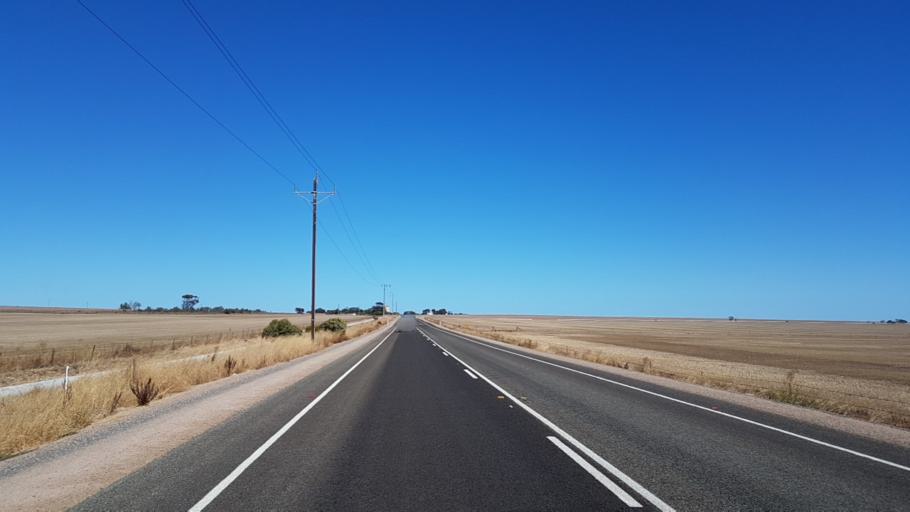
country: AU
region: South Australia
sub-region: Copper Coast
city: Kadina
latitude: -34.0423
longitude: 137.9284
